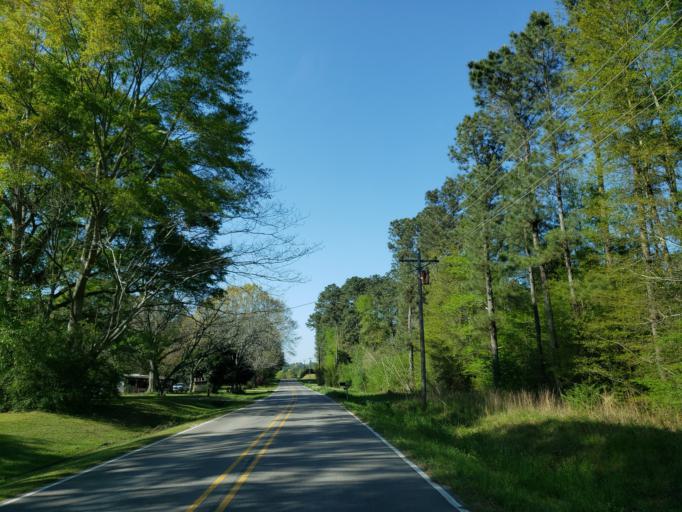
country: US
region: Mississippi
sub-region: Forrest County
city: Rawls Springs
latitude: 31.5443
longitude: -89.3652
